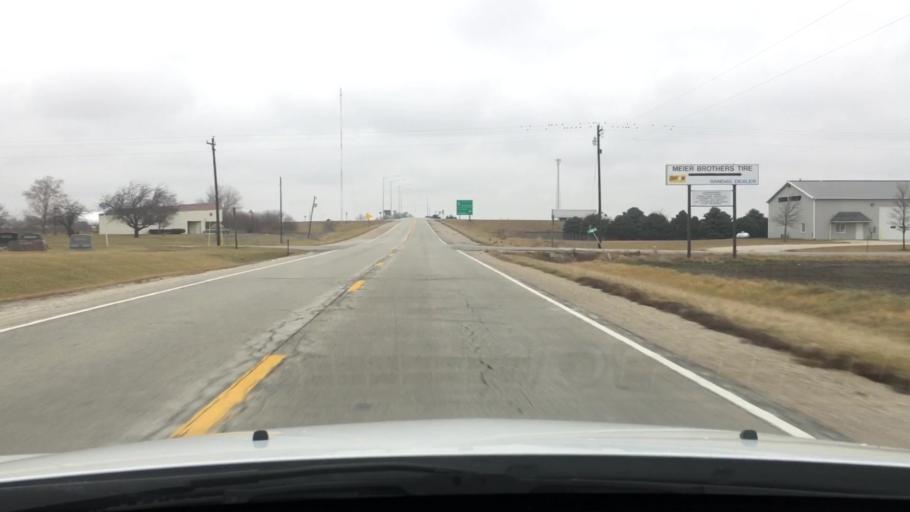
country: US
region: Illinois
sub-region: Iroquois County
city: Clifton
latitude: 40.8843
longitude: -87.9614
